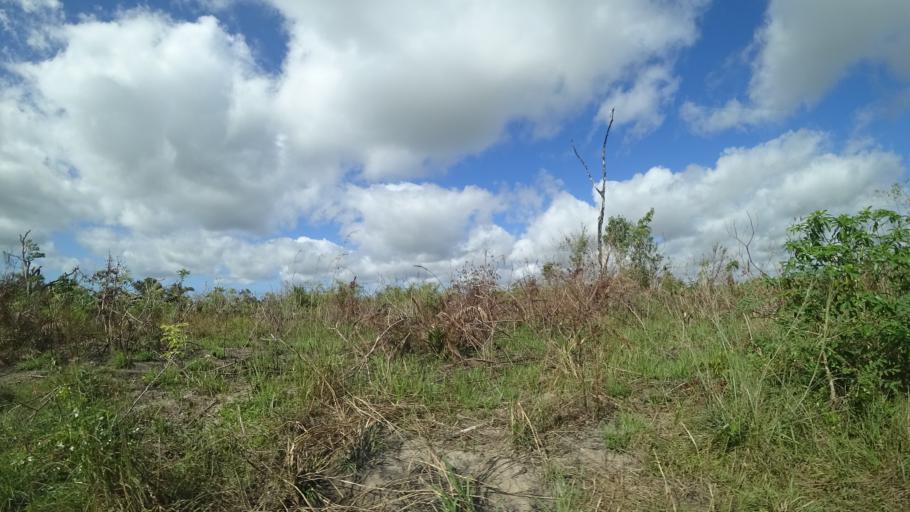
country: MZ
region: Sofala
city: Dondo
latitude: -19.5742
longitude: 35.1016
